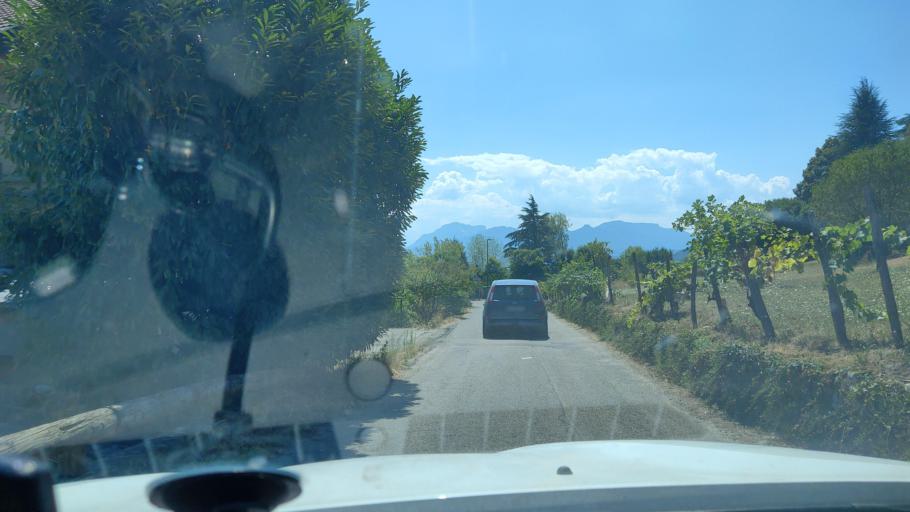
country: FR
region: Rhone-Alpes
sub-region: Departement de la Savoie
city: Le Bourget-du-Lac
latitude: 45.6587
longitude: 5.8506
